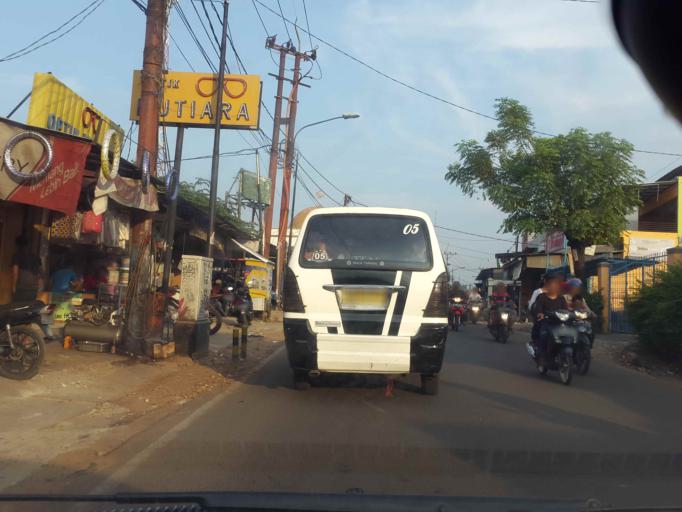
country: ID
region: Banten
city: South Tangerang
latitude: -6.2594
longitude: 106.7441
